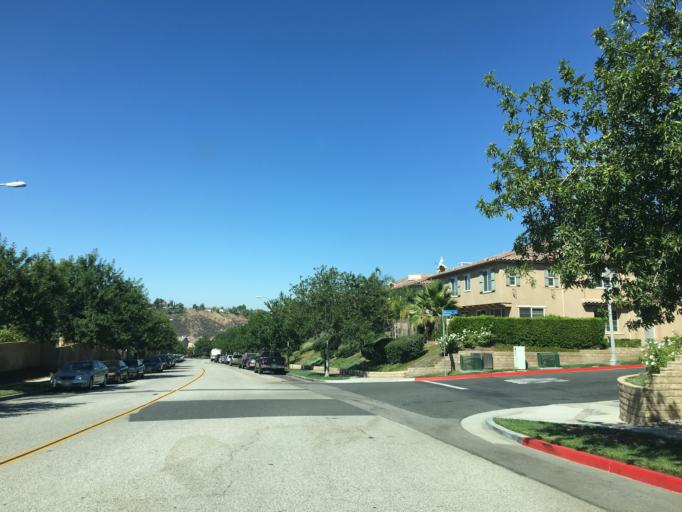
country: US
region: California
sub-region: Los Angeles County
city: Santa Clarita
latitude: 34.4441
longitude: -118.4739
